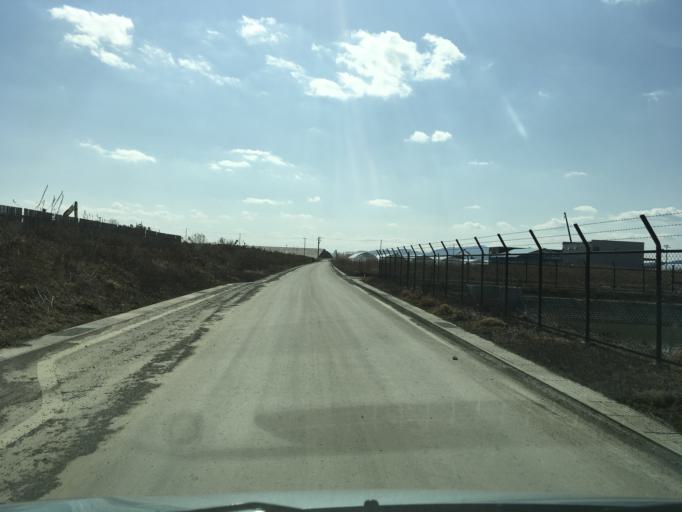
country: JP
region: Iwate
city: Ofunato
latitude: 38.8270
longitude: 141.5922
